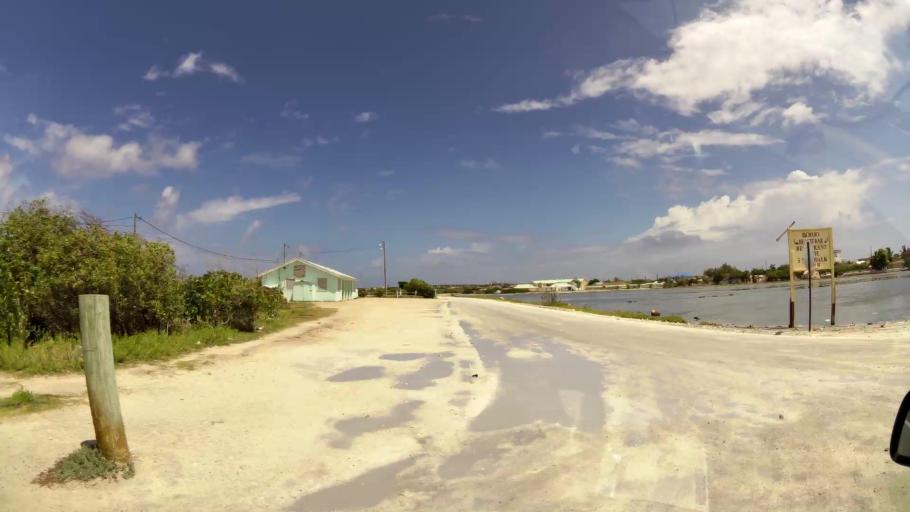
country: TC
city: Cockburn Town
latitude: 21.4782
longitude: -71.1470
